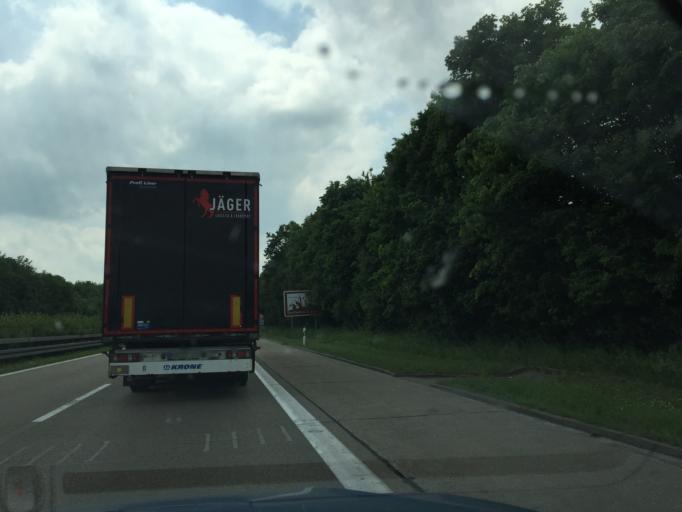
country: DE
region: Baden-Wuerttemberg
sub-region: Regierungsbezirk Stuttgart
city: Herbrechtingen
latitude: 48.5847
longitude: 10.1780
